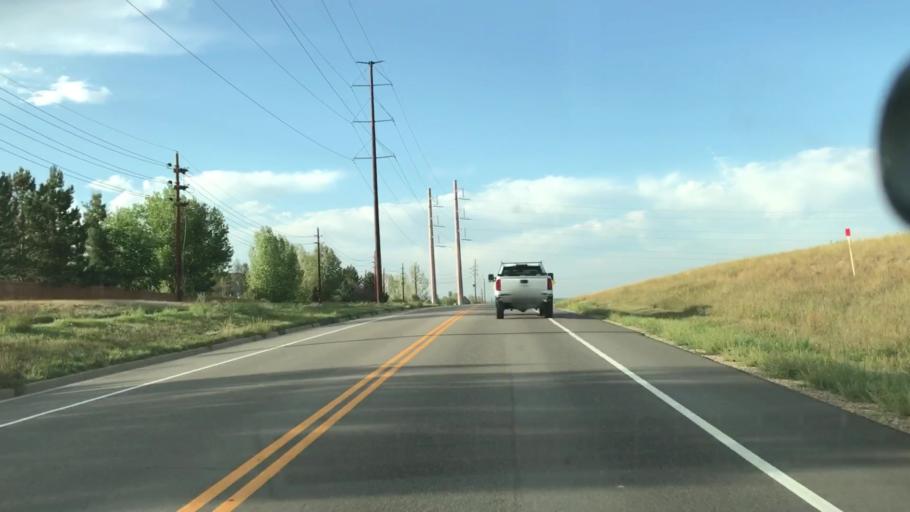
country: US
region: Colorado
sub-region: Boulder County
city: Gunbarrel
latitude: 40.0709
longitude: -105.1785
